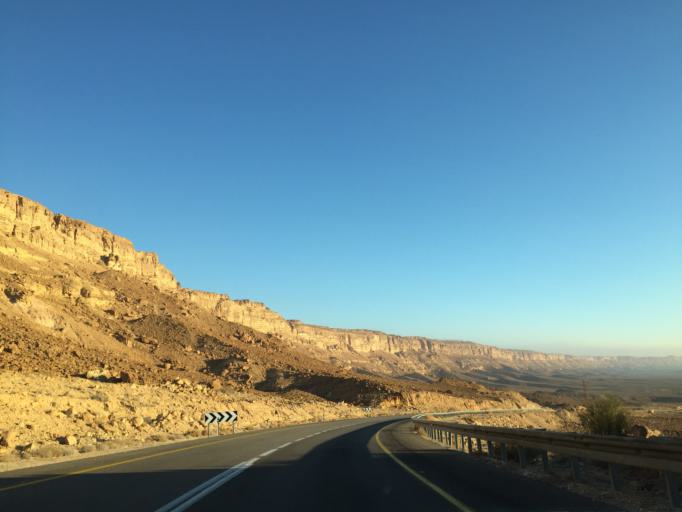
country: IL
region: Southern District
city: Mitzpe Ramon
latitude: 30.6213
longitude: 34.8194
